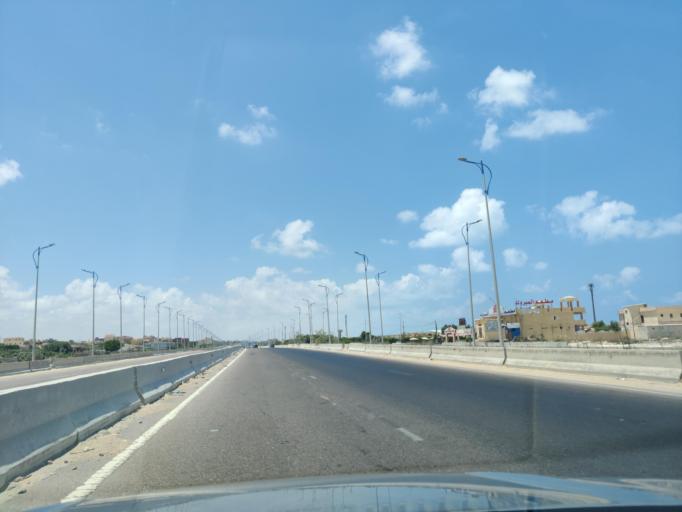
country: EG
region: Alexandria
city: Alexandria
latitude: 30.9810
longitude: 29.5787
